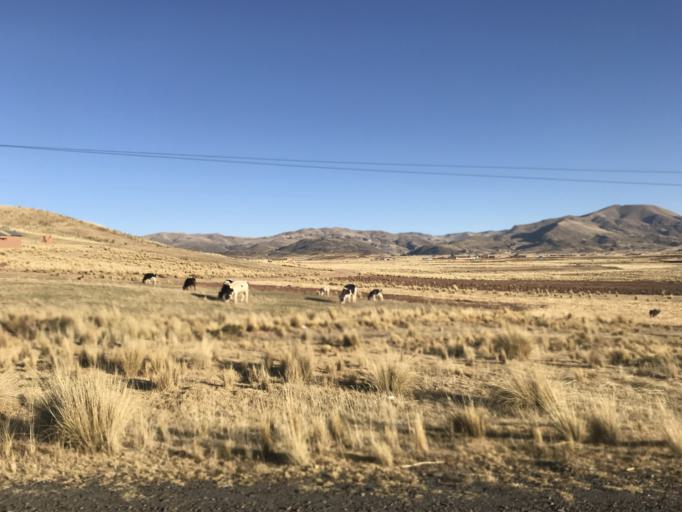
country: BO
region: La Paz
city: Tiahuanaco
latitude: -16.5666
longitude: -68.6472
